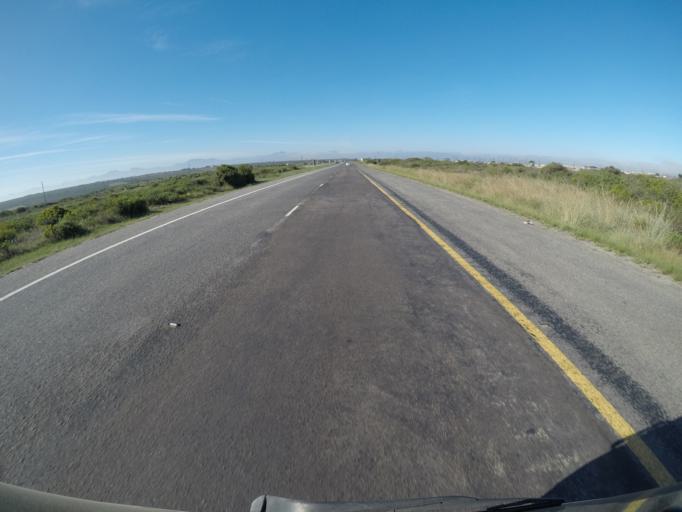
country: ZA
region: Western Cape
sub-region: Eden District Municipality
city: Mossel Bay
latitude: -34.1800
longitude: 22.0620
